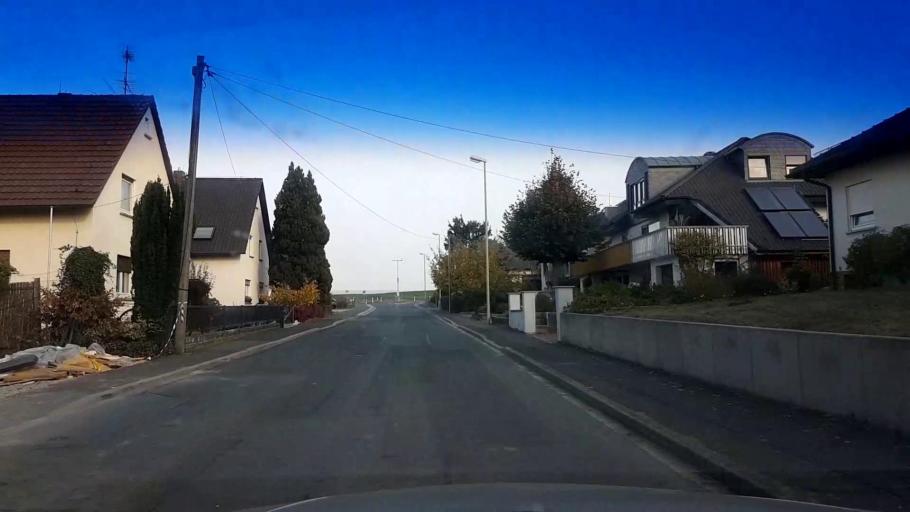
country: DE
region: Bavaria
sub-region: Upper Franconia
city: Altenkunstadt
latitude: 50.1106
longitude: 11.2540
